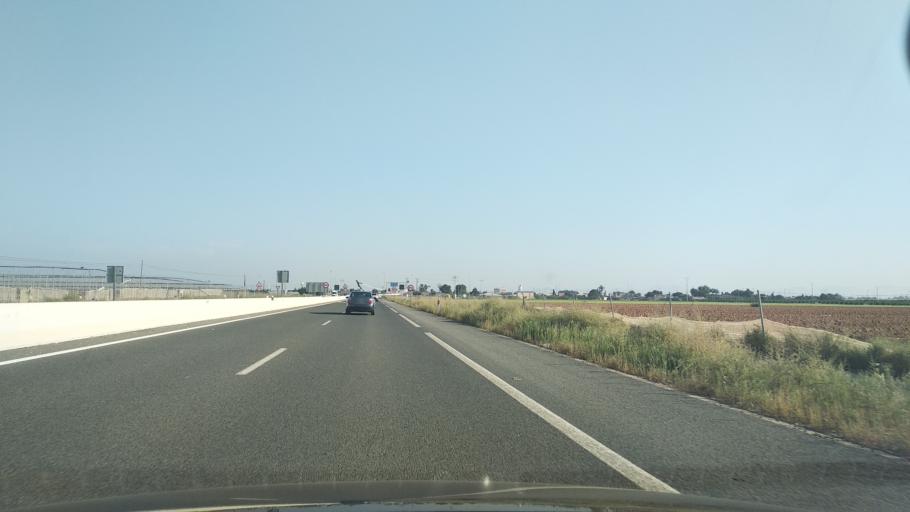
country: ES
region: Murcia
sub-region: Murcia
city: San Javier
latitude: 37.8244
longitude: -0.8525
